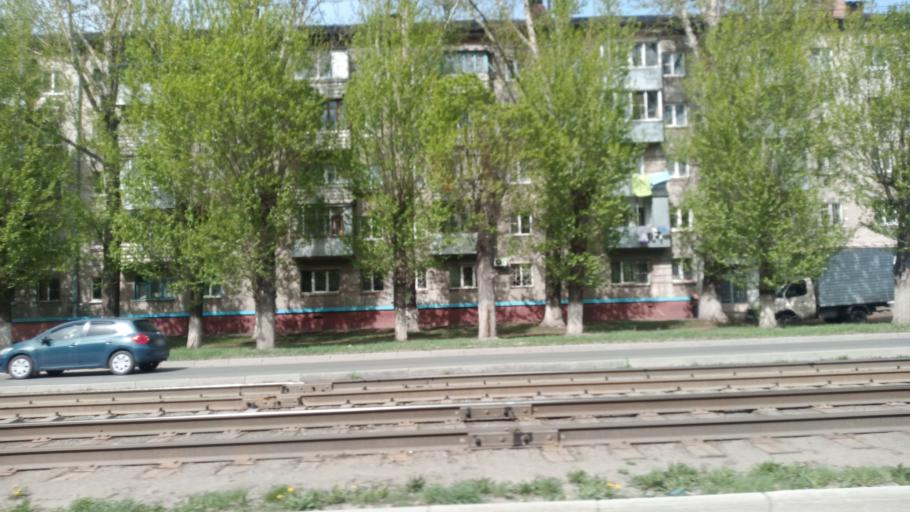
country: RU
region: Altai Krai
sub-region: Gorod Barnaulskiy
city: Barnaul
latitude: 53.3593
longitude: 83.7258
